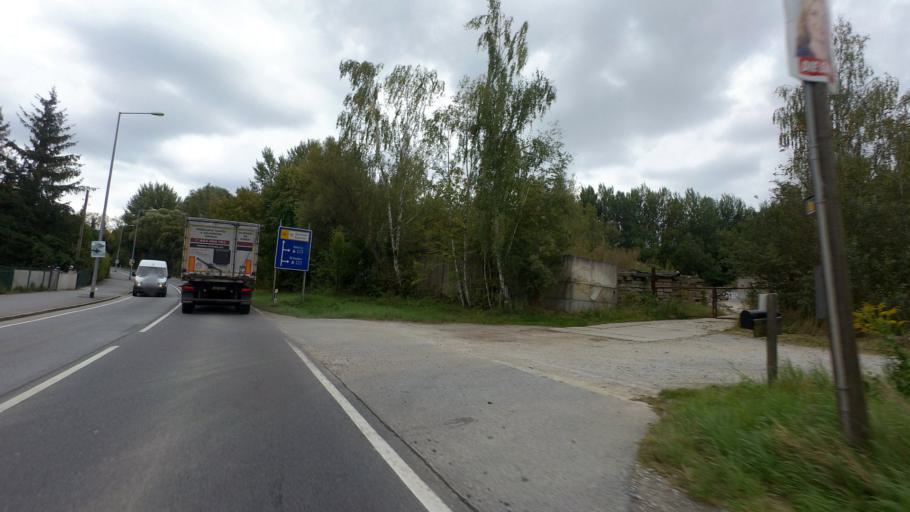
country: DE
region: Saxony
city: Bautzen
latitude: 51.1937
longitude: 14.4100
